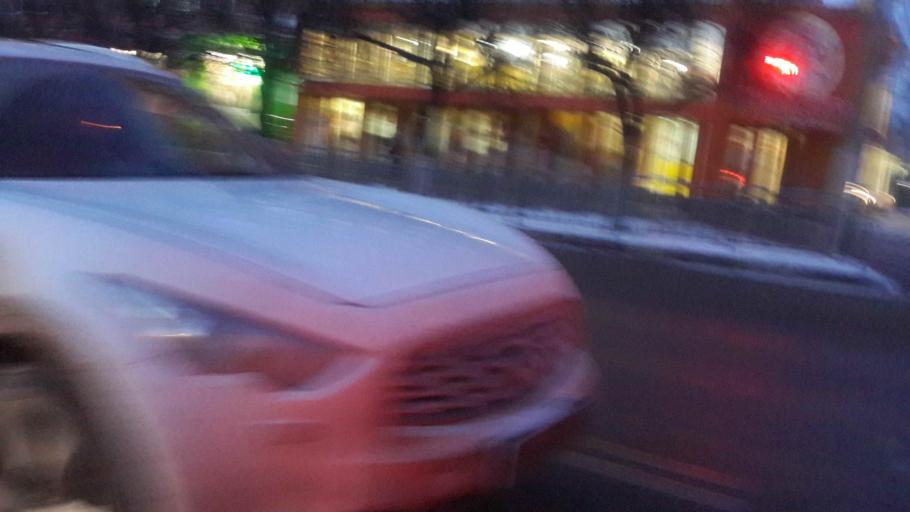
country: RU
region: Tula
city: Tula
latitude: 54.1965
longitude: 37.6065
